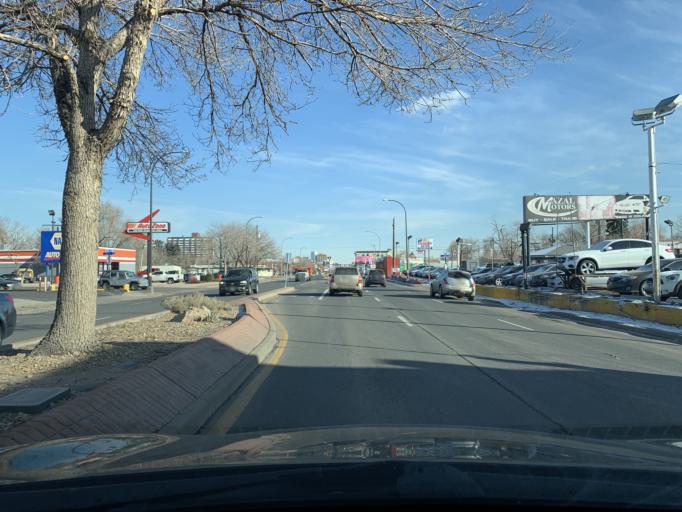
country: US
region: Colorado
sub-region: Jefferson County
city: Edgewater
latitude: 39.7404
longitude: -105.0574
